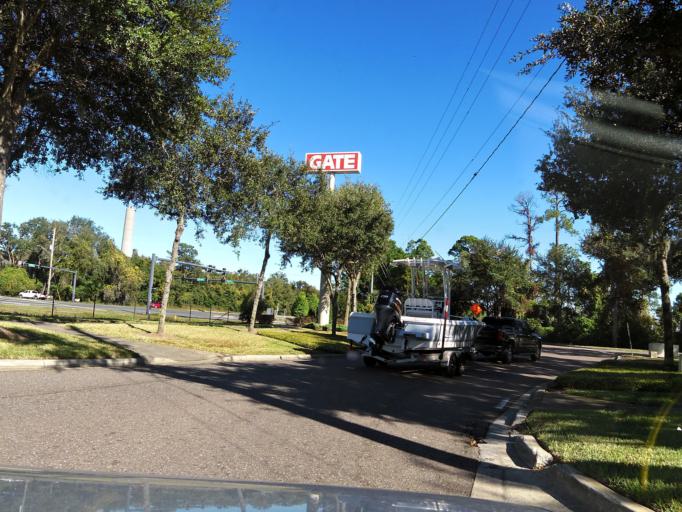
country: US
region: Florida
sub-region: Duval County
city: Jacksonville
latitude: 30.4116
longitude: -81.5615
